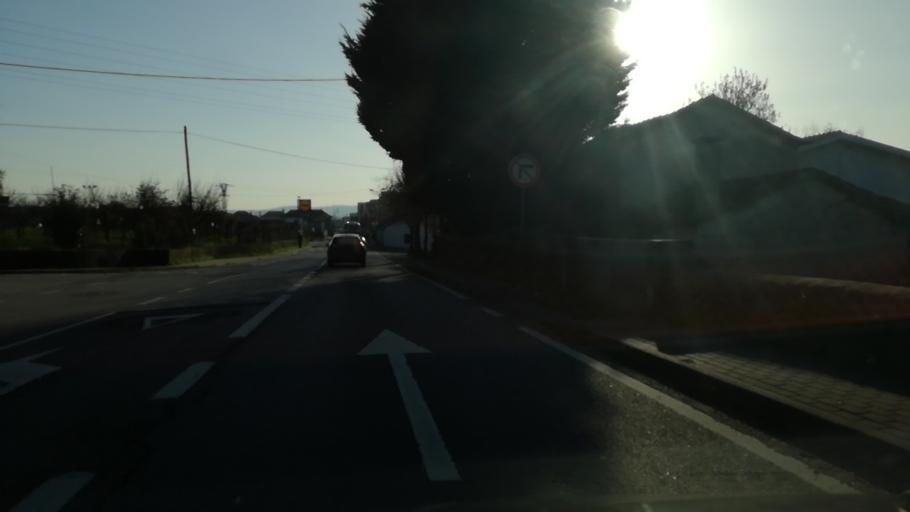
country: PT
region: Braga
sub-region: Vila Nova de Famalicao
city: Ferreiros
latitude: 41.3550
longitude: -8.5529
